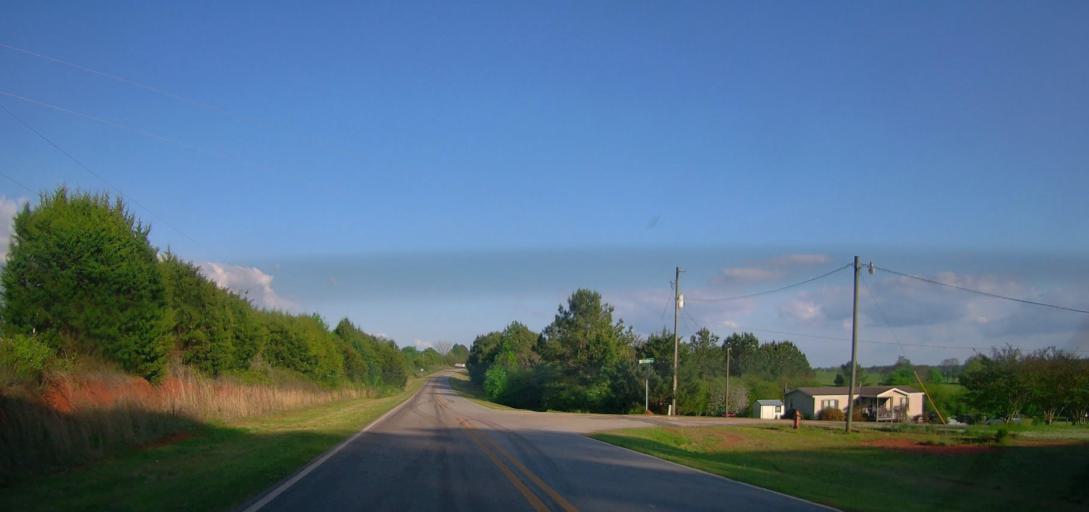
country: US
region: Georgia
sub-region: Putnam County
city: Eatonton
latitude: 33.3125
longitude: -83.3599
